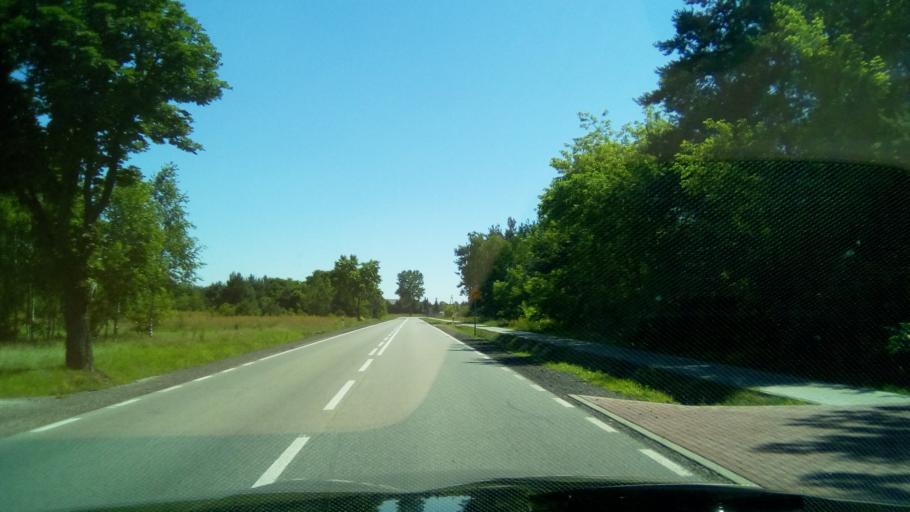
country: PL
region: Masovian Voivodeship
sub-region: Powiat przysuski
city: Odrzywol
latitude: 51.5175
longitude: 20.5424
